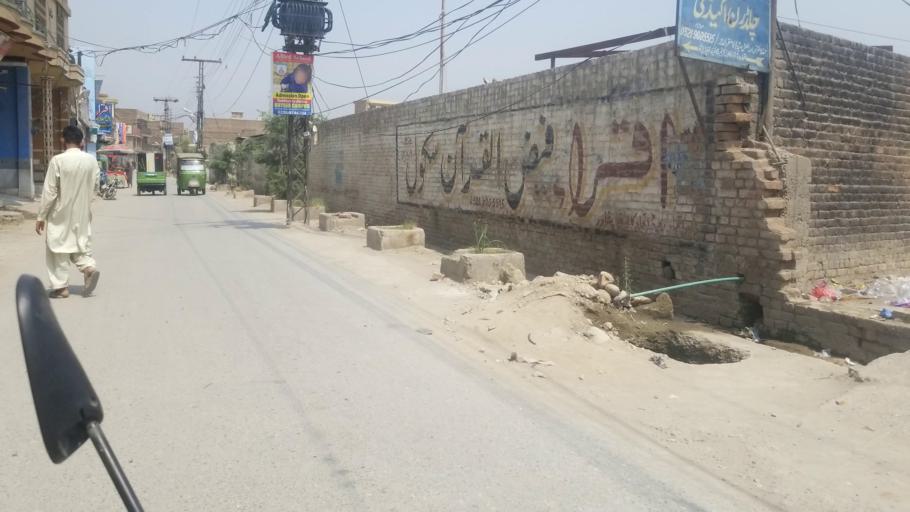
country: PK
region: Khyber Pakhtunkhwa
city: Peshawar
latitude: 34.0265
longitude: 71.5884
